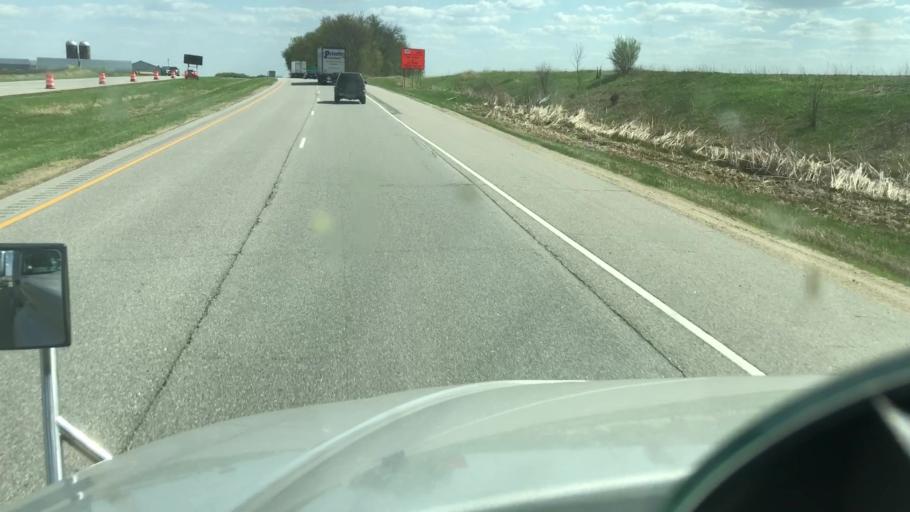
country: US
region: Minnesota
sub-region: Le Sueur County
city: Le Sueur
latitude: 44.5412
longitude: -93.8495
